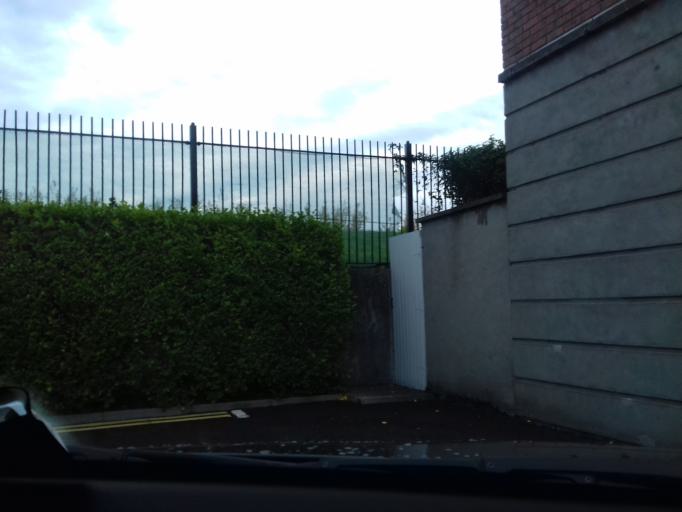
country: IE
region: Leinster
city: Cabra
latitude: 53.3656
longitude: -6.2772
